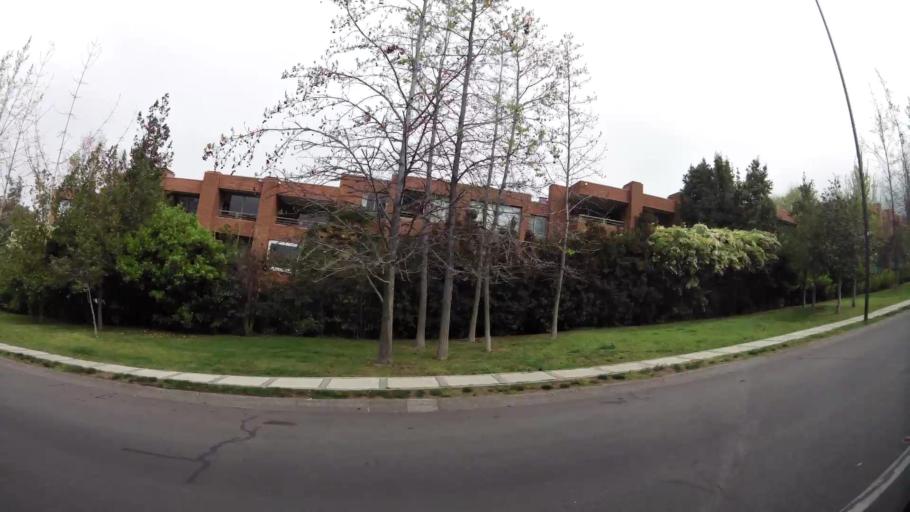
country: CL
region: Santiago Metropolitan
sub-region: Provincia de Santiago
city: Villa Presidente Frei, Nunoa, Santiago, Chile
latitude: -33.3686
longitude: -70.5777
